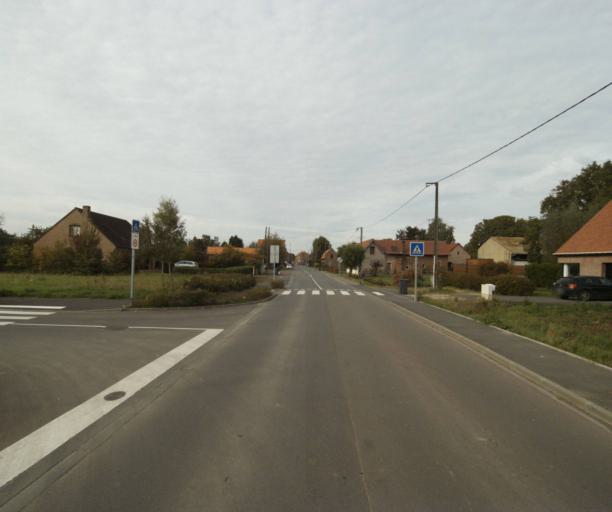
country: FR
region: Nord-Pas-de-Calais
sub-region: Departement du Nord
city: Herlies
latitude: 50.6076
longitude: 2.8601
